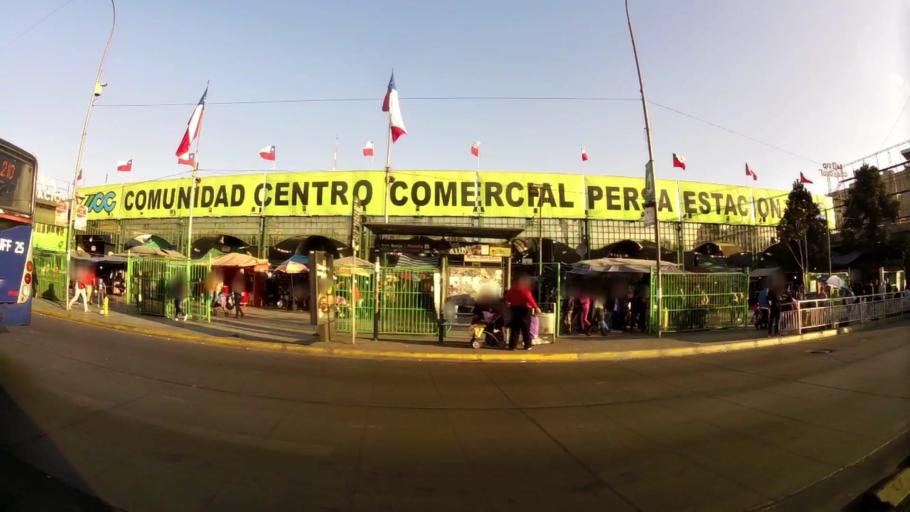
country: CL
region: Santiago Metropolitan
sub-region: Provincia de Santiago
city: Santiago
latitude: -33.4517
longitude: -70.6810
